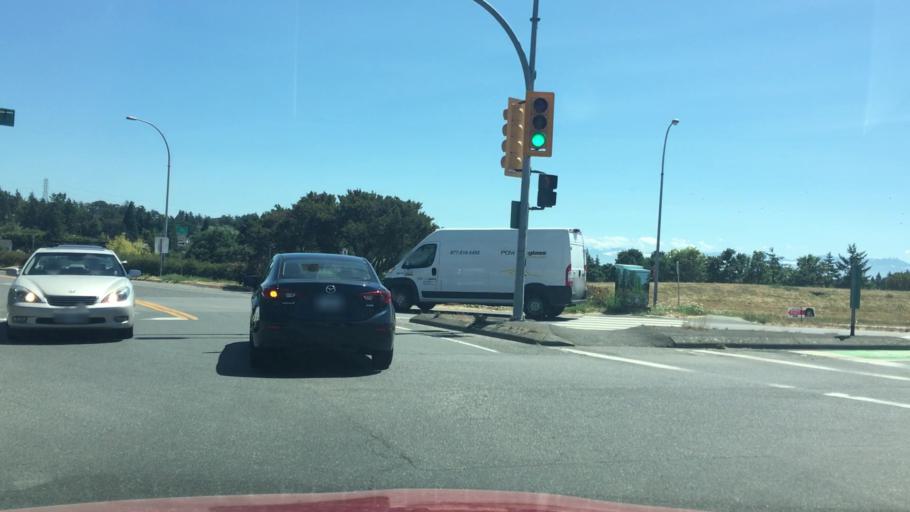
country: CA
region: British Columbia
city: Victoria
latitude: 48.4876
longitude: -123.3867
